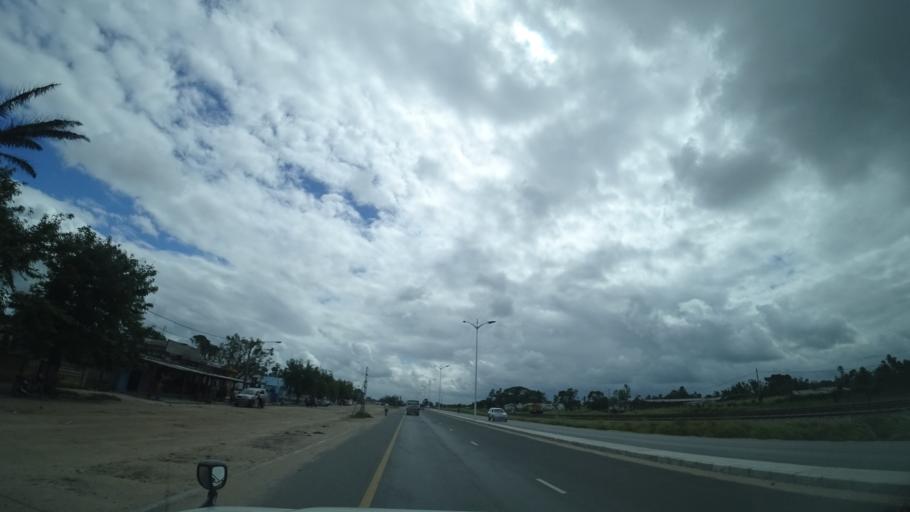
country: MZ
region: Sofala
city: Dondo
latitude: -19.6170
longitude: 34.7460
